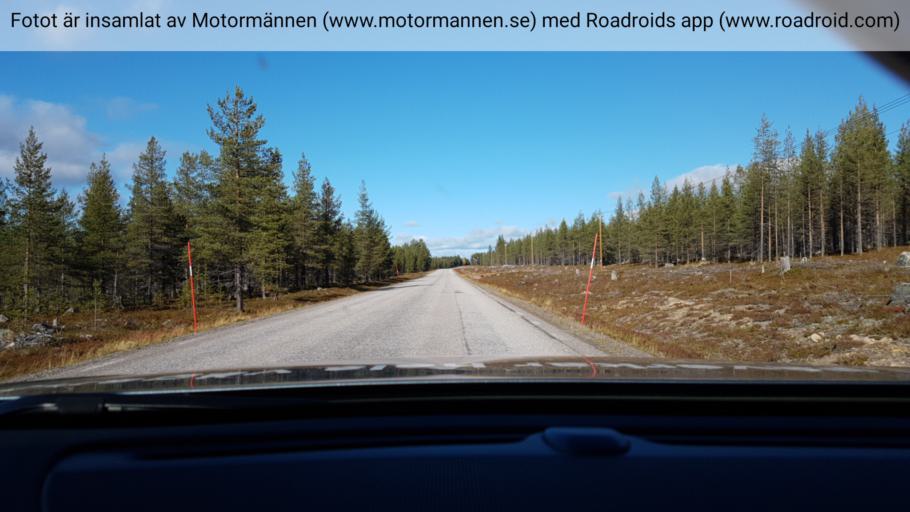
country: SE
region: Vaesterbotten
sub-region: Mala Kommun
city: Mala
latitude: 65.7787
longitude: 18.5096
